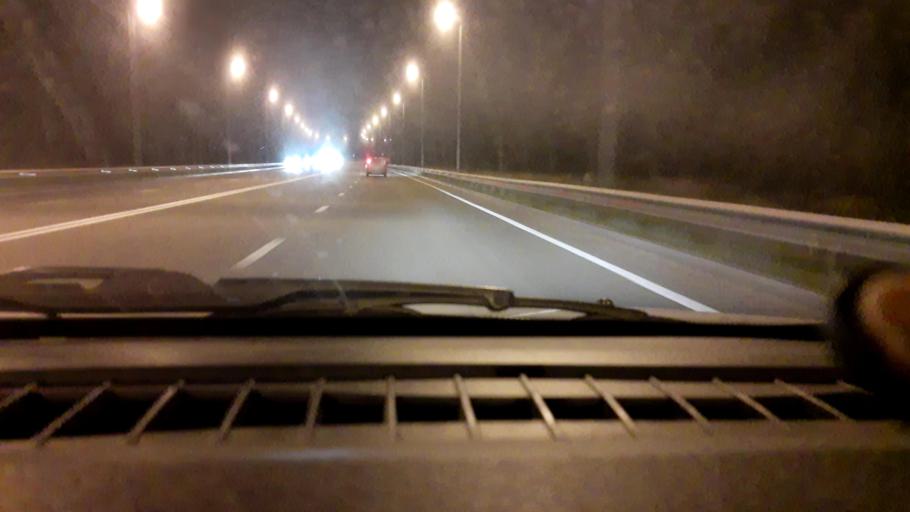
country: RU
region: Nizjnij Novgorod
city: Gorbatovka
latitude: 56.2341
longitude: 43.8072
